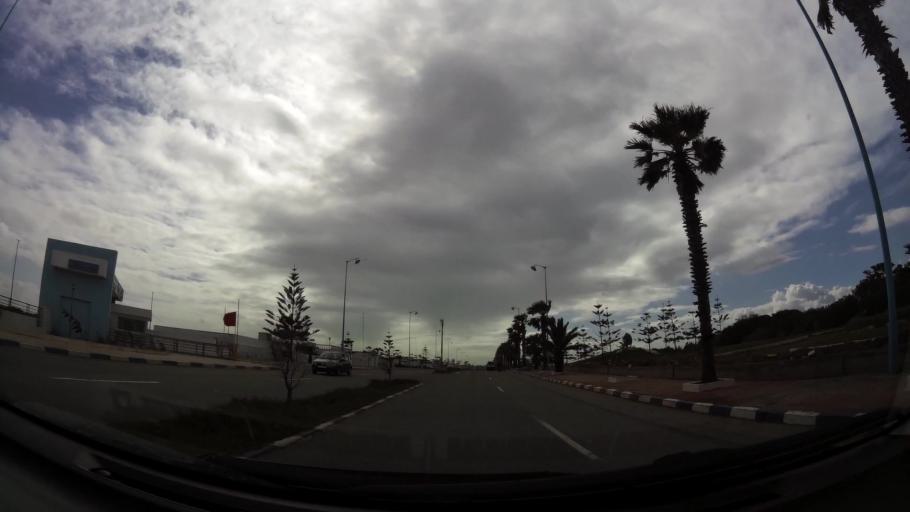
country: MA
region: Doukkala-Abda
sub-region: El-Jadida
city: El Jadida
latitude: 33.2442
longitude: -8.4653
